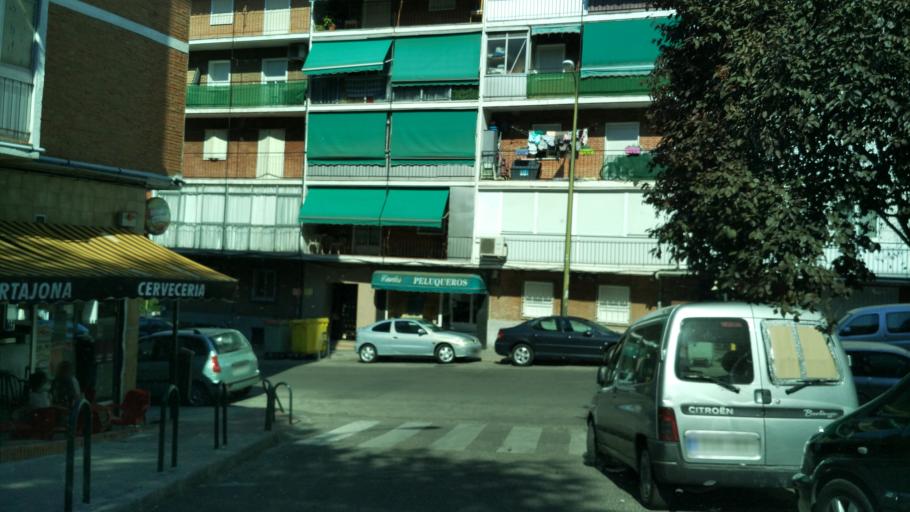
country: ES
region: Madrid
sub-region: Provincia de Madrid
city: Tetuan de las Victorias
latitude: 40.4642
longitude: -3.7180
